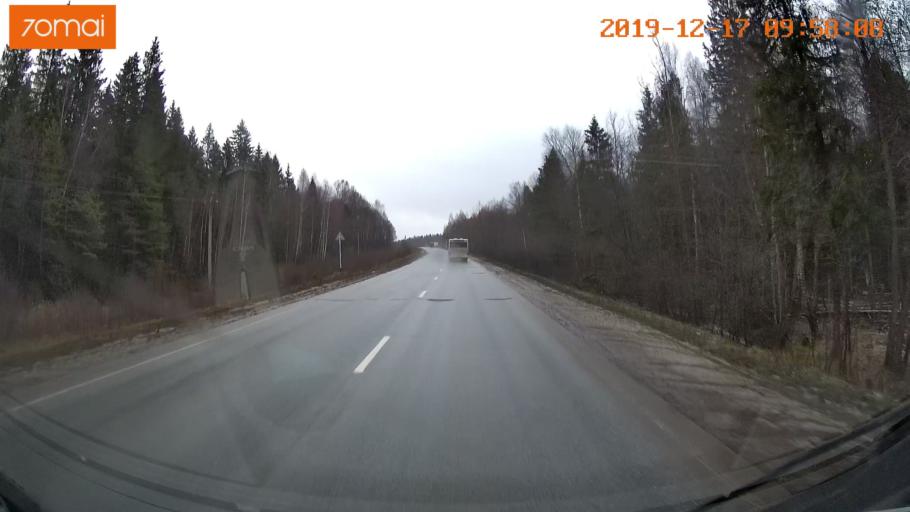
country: RU
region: Vladimir
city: Golovino
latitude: 55.9719
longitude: 40.5481
